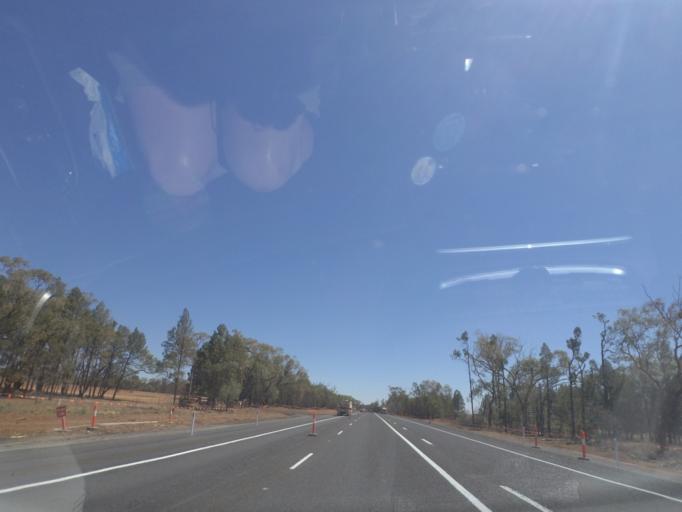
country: AU
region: New South Wales
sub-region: Gilgandra
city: Gilgandra
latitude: -31.6616
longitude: 148.7219
